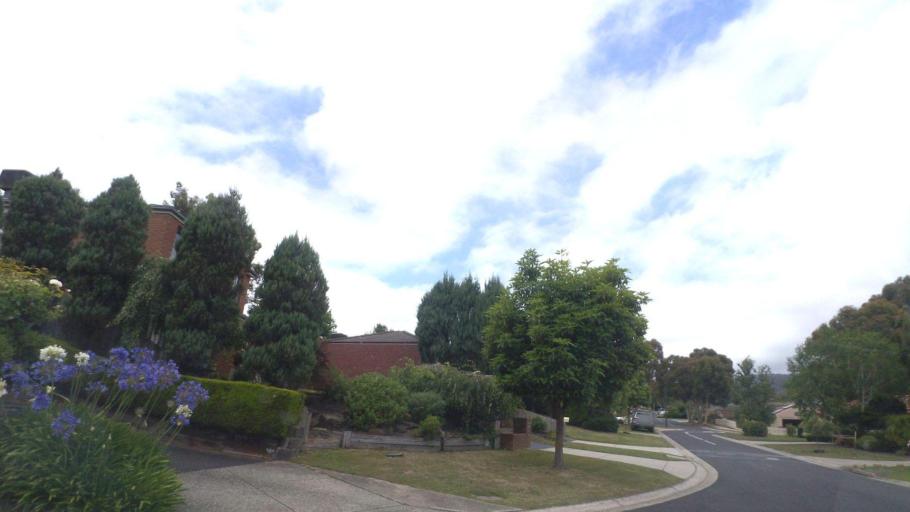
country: AU
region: Victoria
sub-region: Knox
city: The Basin
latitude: -37.8509
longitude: 145.3101
